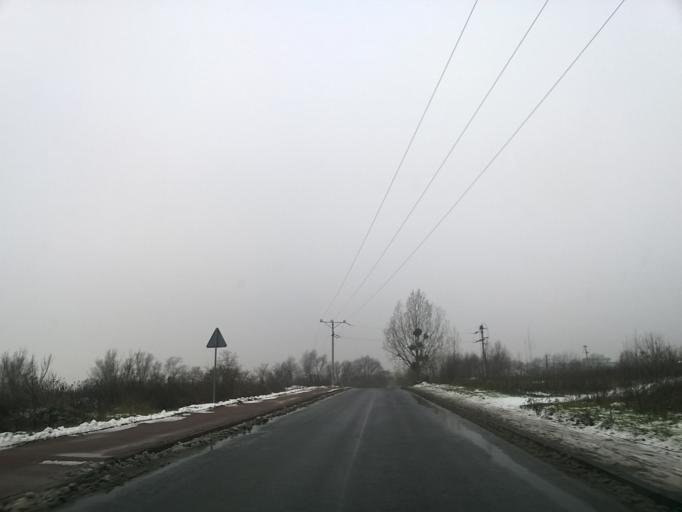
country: PL
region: Kujawsko-Pomorskie
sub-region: Powiat swiecki
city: Swiecie
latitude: 53.4025
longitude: 18.4373
